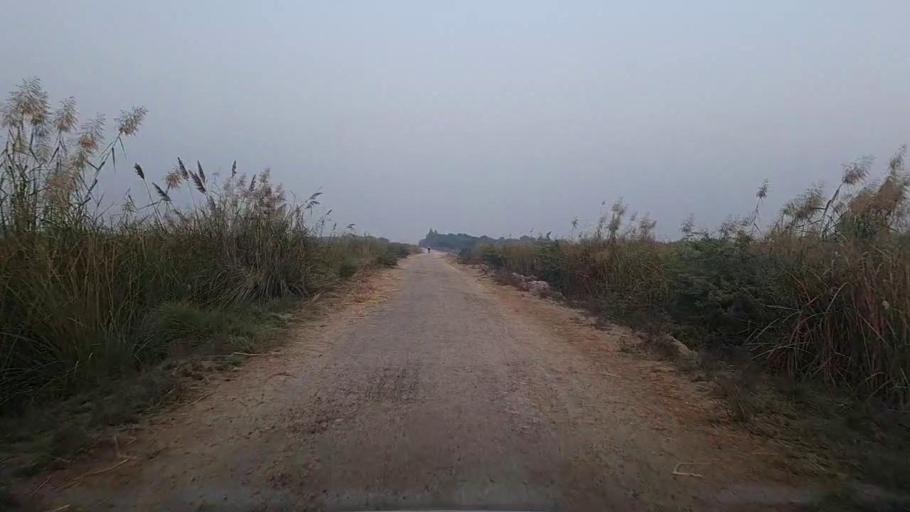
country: PK
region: Sindh
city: Kot Diji
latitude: 27.3432
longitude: 68.6309
